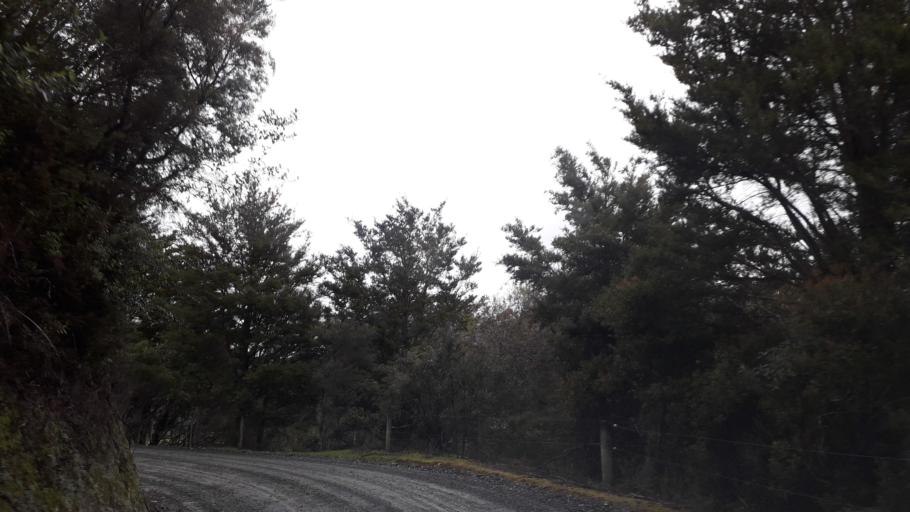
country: NZ
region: Northland
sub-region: Far North District
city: Waimate North
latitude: -35.1600
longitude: 173.7135
